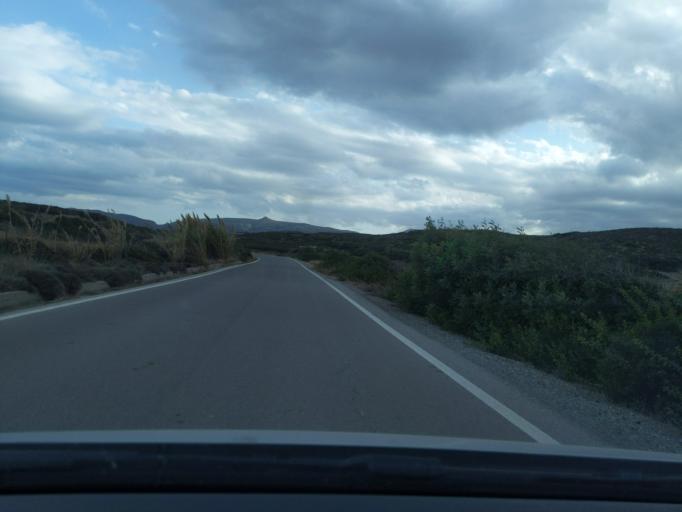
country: GR
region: Crete
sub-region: Nomos Lasithiou
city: Palekastro
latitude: 35.2405
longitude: 26.2481
